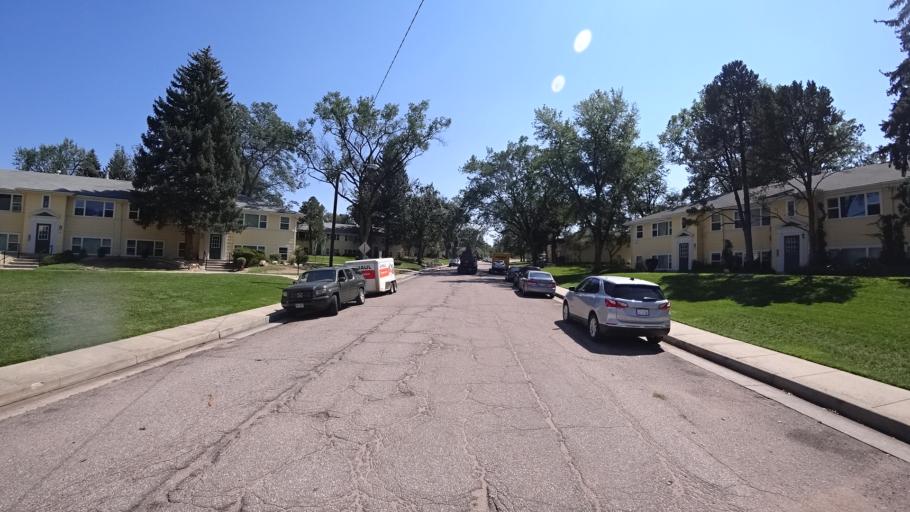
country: US
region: Colorado
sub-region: El Paso County
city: Colorado Springs
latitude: 38.8513
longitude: -104.8021
